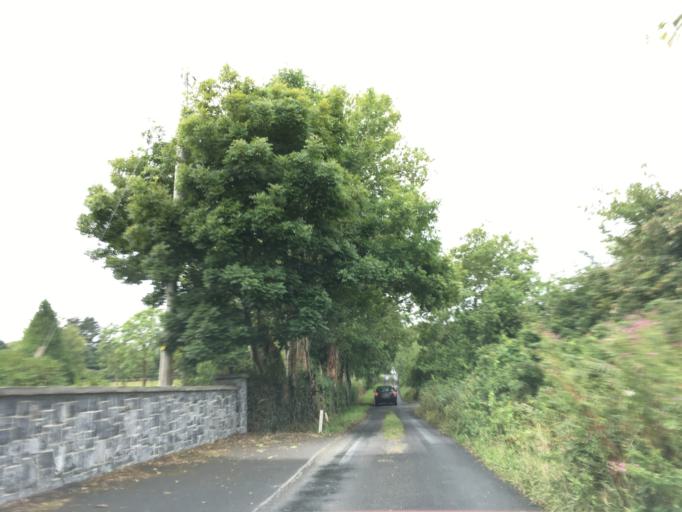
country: IE
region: Munster
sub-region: An Clar
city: Ennis
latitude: 52.7289
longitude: -9.0843
